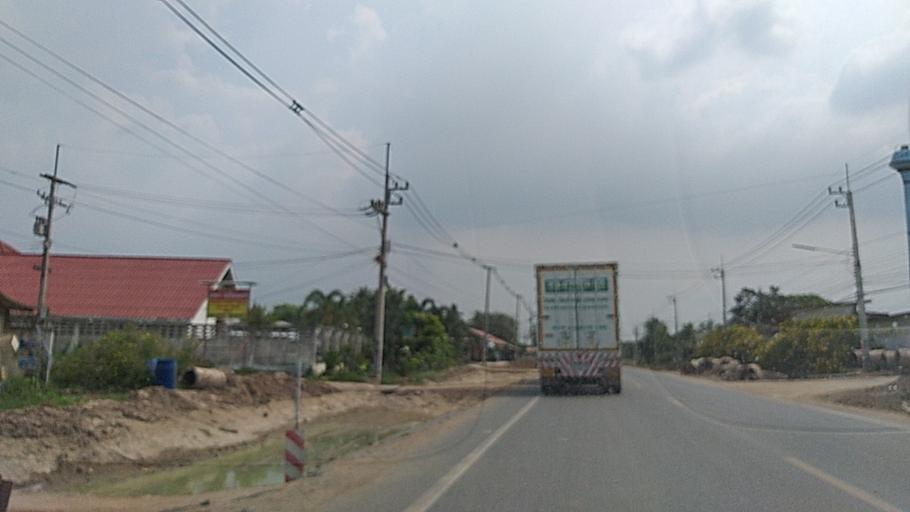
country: TH
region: Chon Buri
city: Ban Bueng
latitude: 13.3508
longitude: 101.1954
